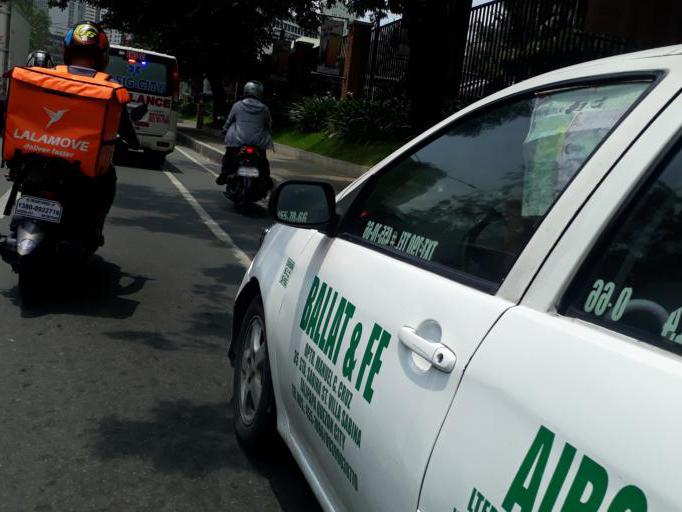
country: PH
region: Metro Manila
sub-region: Pasig
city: Pasig City
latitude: 14.5892
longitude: 121.0683
